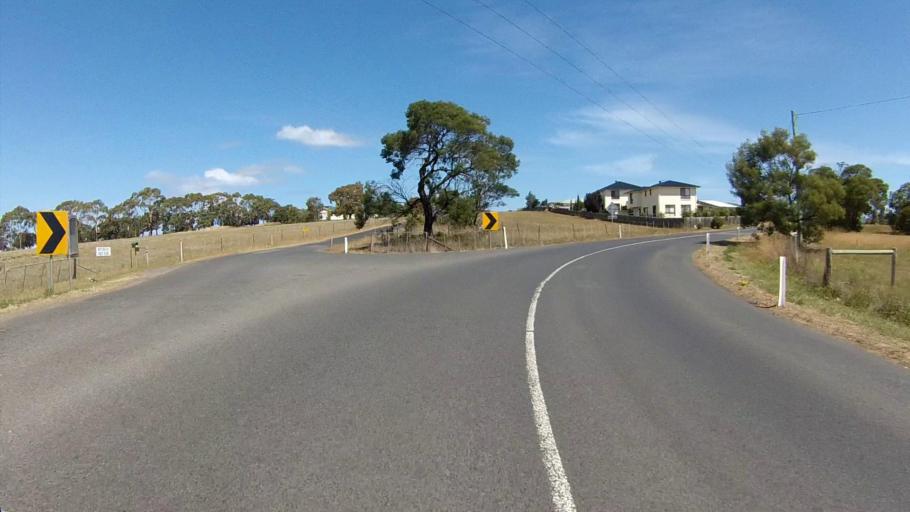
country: AU
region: Tasmania
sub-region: Sorell
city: Sorell
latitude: -42.7813
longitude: 147.5245
